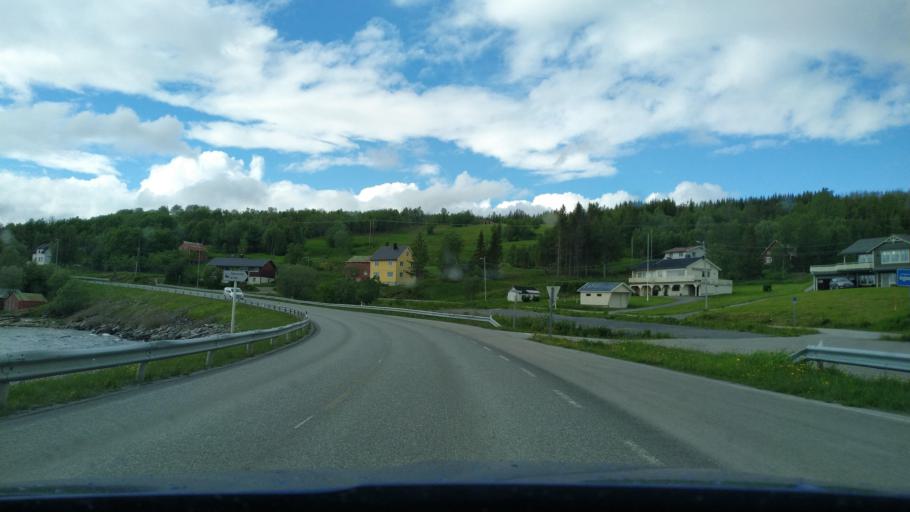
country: NO
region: Troms
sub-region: Sorreisa
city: Sorreisa
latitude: 69.1759
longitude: 18.0826
